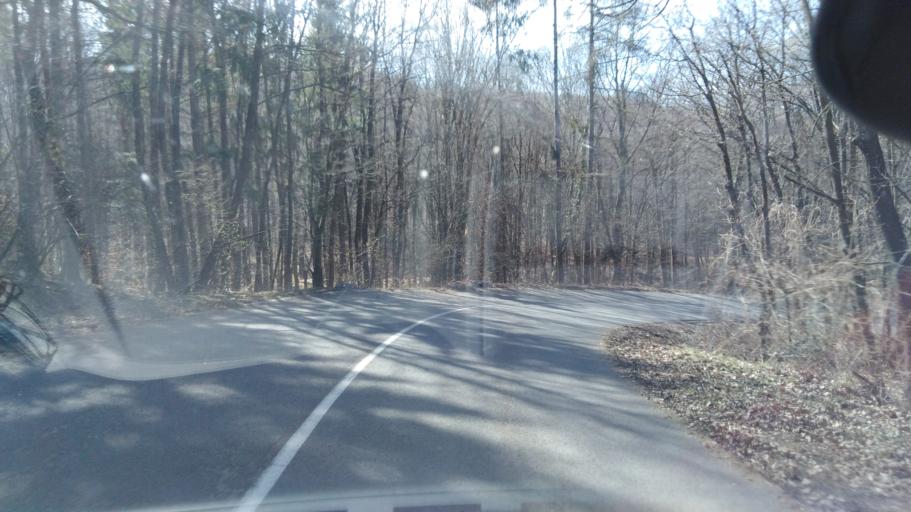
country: HU
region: Nograd
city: Somoskoujfalu
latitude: 48.1546
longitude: 19.8538
